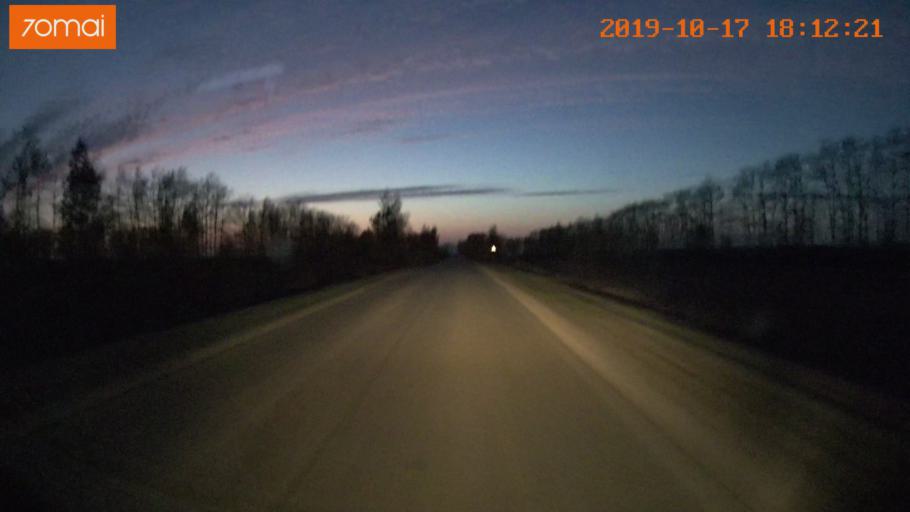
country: RU
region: Tula
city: Kurkino
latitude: 53.4118
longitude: 38.6132
